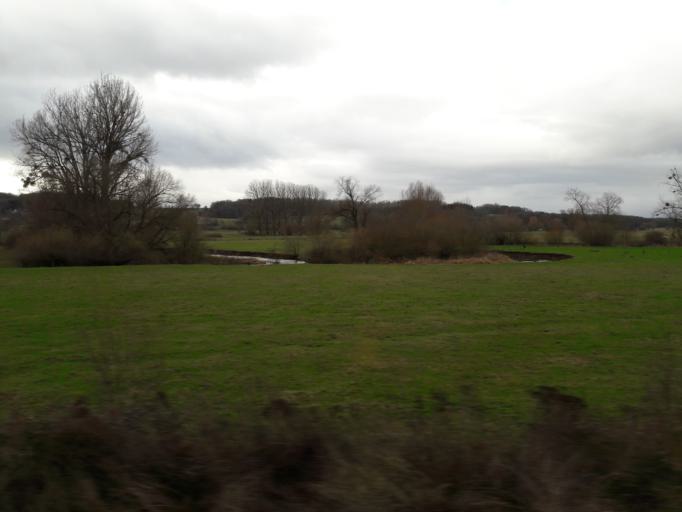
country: FR
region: Franche-Comte
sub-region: Territoire de Belfort
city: Joncherey
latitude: 47.5294
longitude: 6.9968
